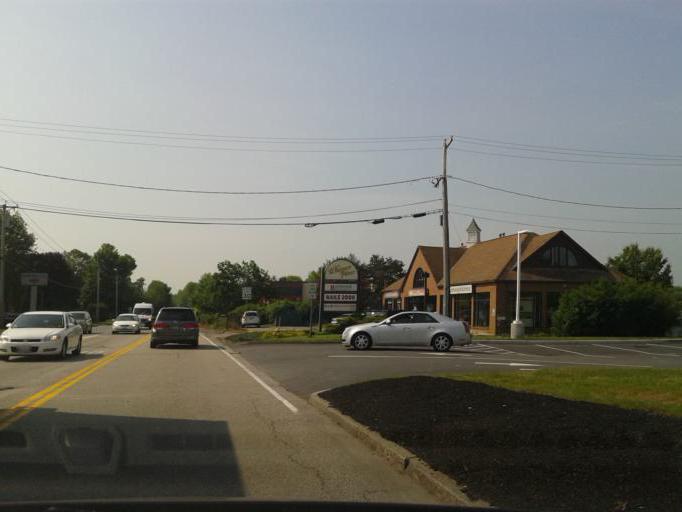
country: US
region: Massachusetts
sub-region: Worcester County
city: Westborough
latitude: 42.2848
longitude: -71.6080
